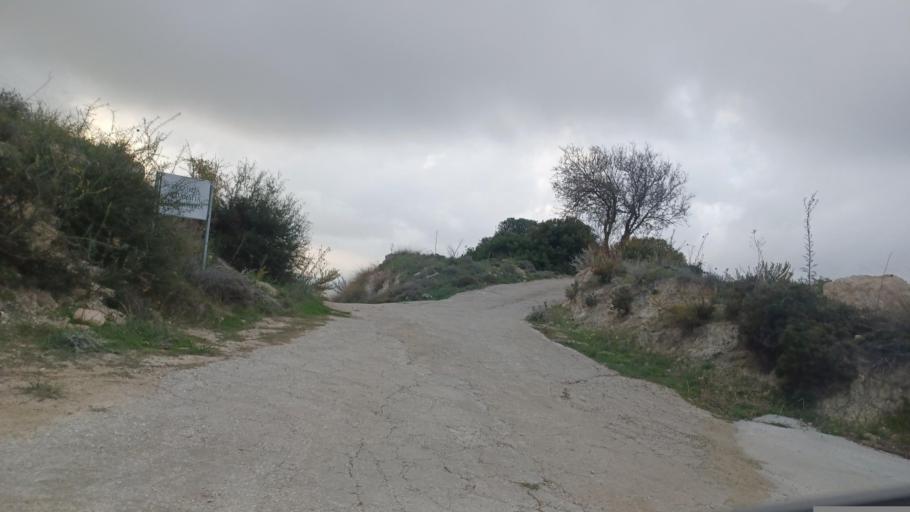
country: CY
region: Pafos
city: Mesogi
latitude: 34.7867
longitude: 32.5058
